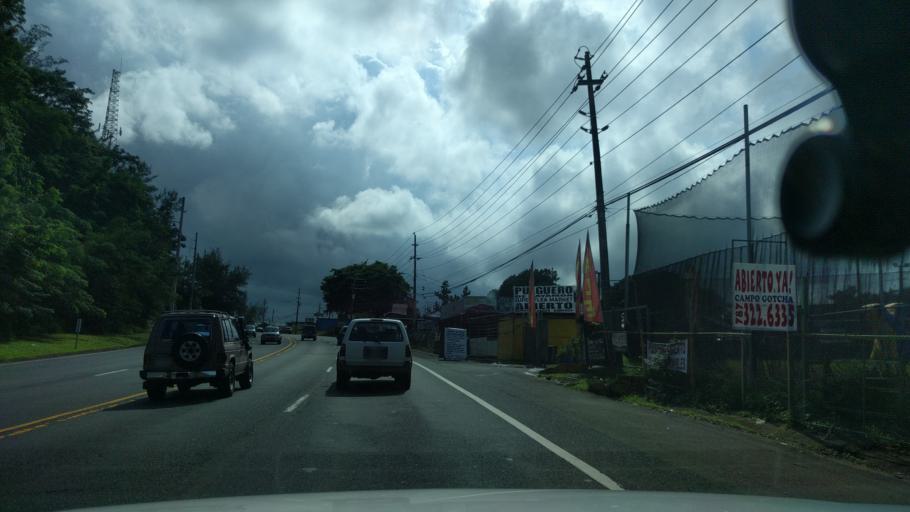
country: PR
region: Toa Alta
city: Pajaros
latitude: 18.3591
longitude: -66.1905
